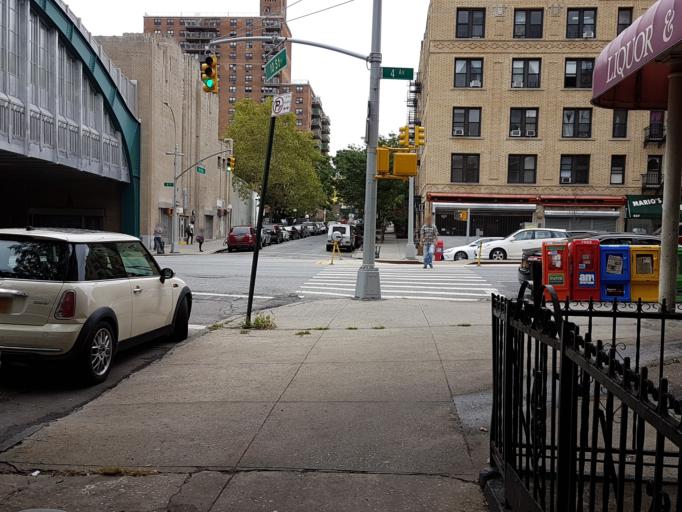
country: US
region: New York
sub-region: Kings County
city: Brooklyn
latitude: 40.6698
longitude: -73.9897
